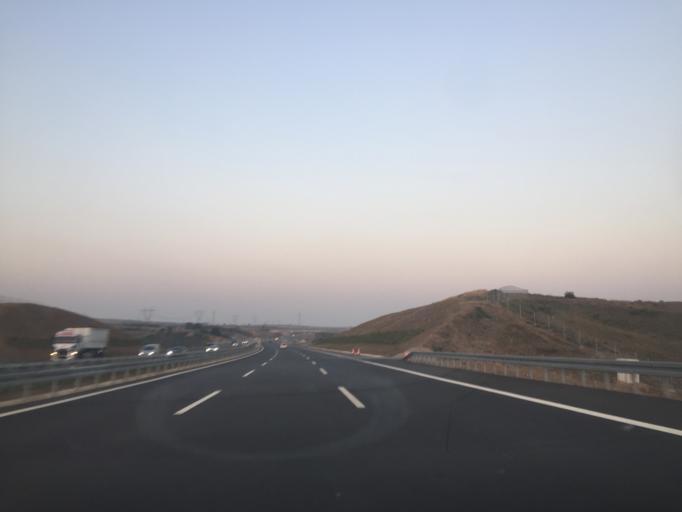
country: TR
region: Bursa
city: Mahmudiye
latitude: 40.2740
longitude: 28.5625
